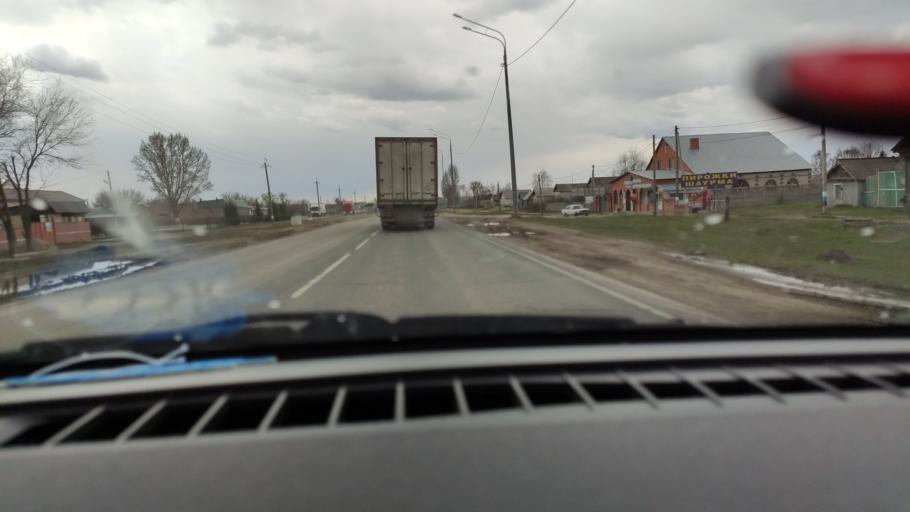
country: RU
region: Saratov
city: Sinodskoye
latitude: 51.9840
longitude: 46.6617
